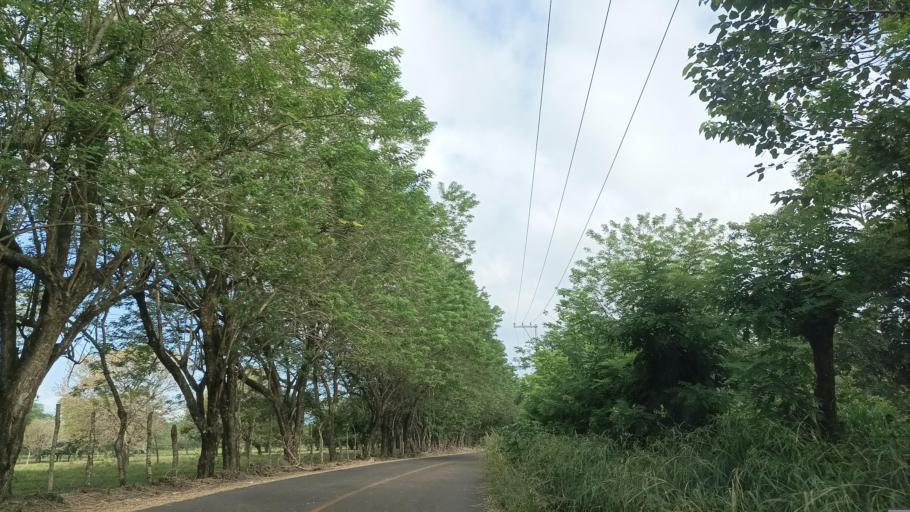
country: MX
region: Veracruz
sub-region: Pajapan
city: Pajapan
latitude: 18.1858
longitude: -94.6904
